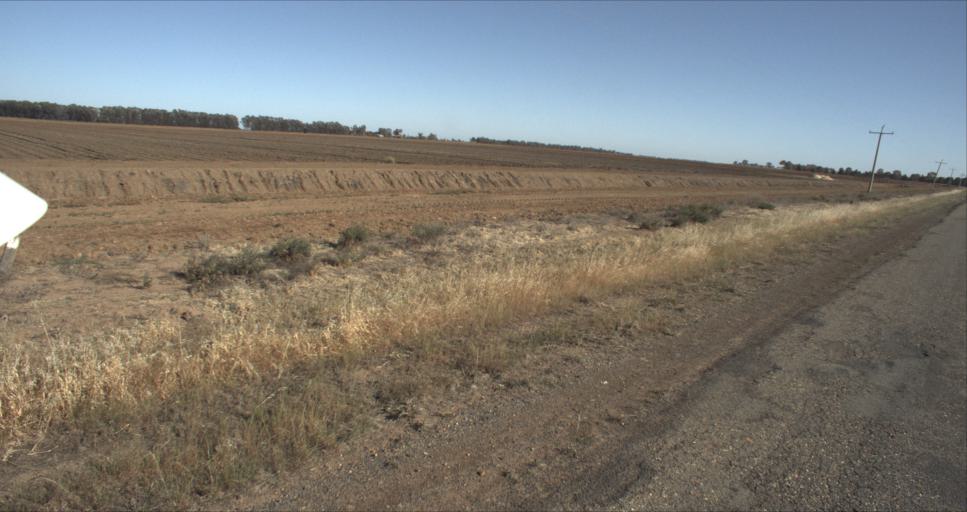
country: AU
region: New South Wales
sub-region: Leeton
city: Leeton
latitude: -34.5966
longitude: 146.2586
